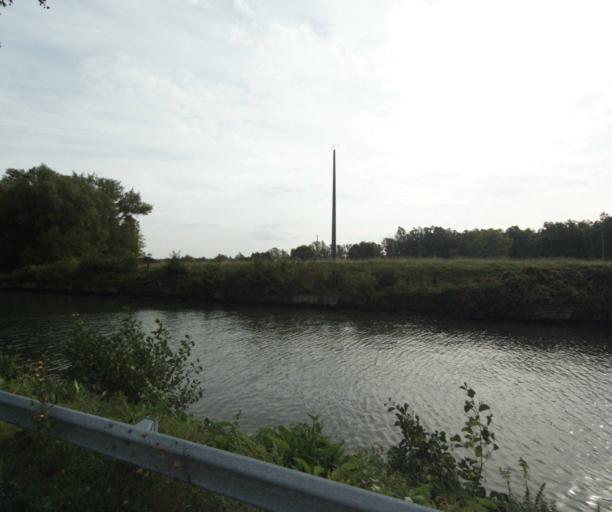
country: FR
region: Nord-Pas-de-Calais
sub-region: Departement du Nord
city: Don
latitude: 50.5446
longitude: 2.9092
